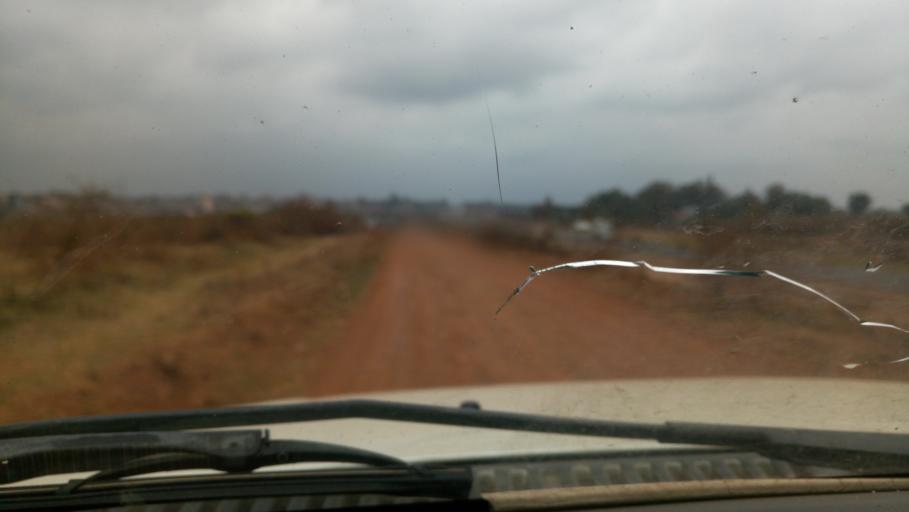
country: KE
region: Kiambu
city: Kiambu
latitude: -1.1986
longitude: 36.8979
